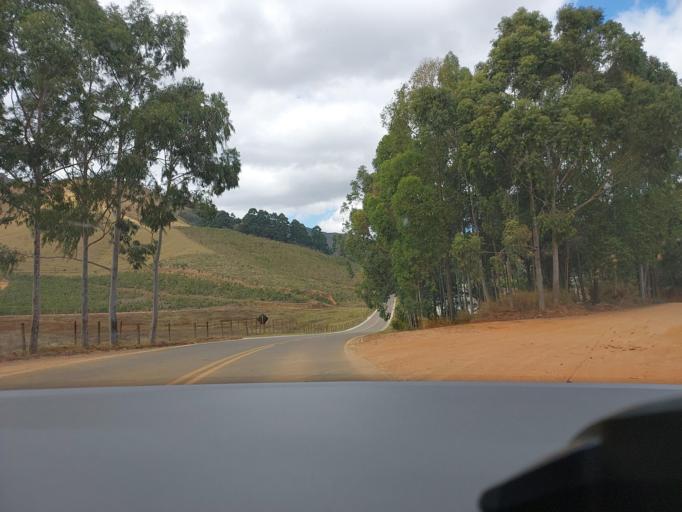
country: BR
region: Minas Gerais
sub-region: Mirai
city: Mirai
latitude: -20.9528
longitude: -42.6043
